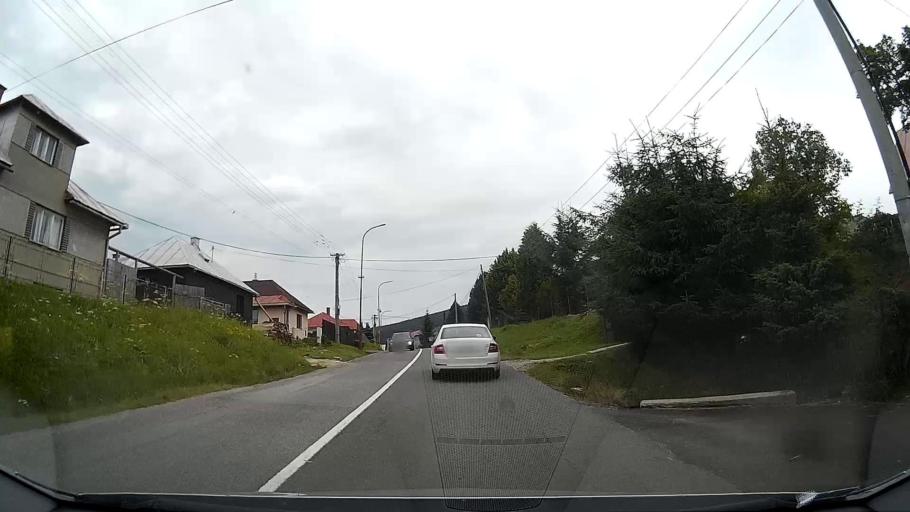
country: SK
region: Kosicky
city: Dobsina
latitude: 48.8513
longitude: 20.1931
